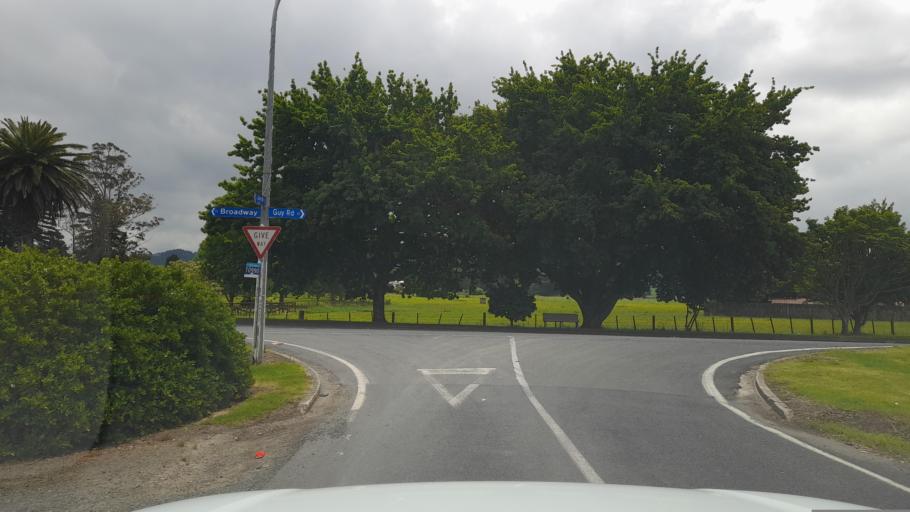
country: NZ
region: Northland
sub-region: Far North District
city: Waimate North
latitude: -35.4032
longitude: 173.8083
